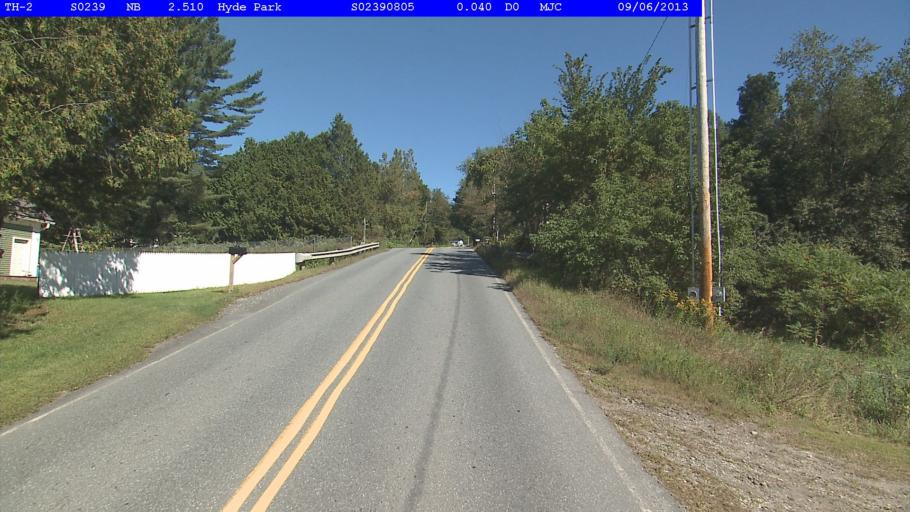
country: US
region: Vermont
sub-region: Lamoille County
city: Hyde Park
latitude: 44.5897
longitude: -72.6144
